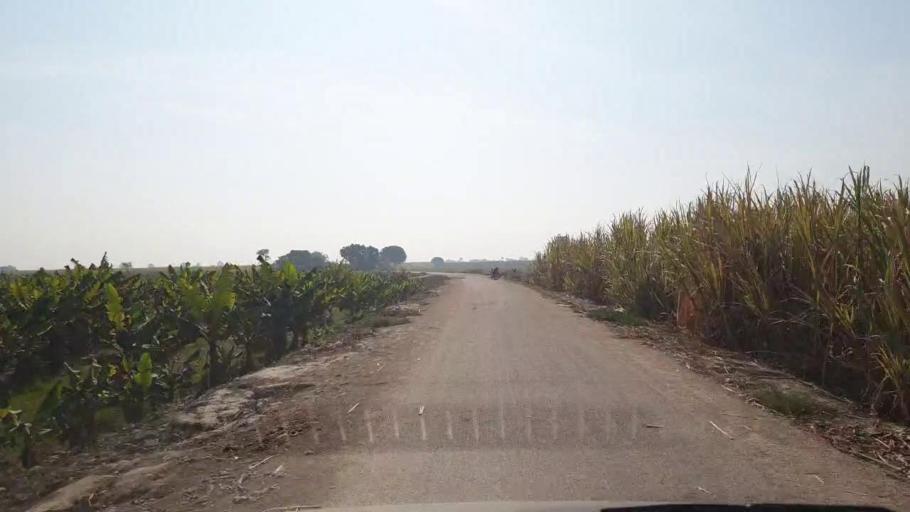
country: PK
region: Sindh
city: Tando Allahyar
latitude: 25.4028
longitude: 68.7402
